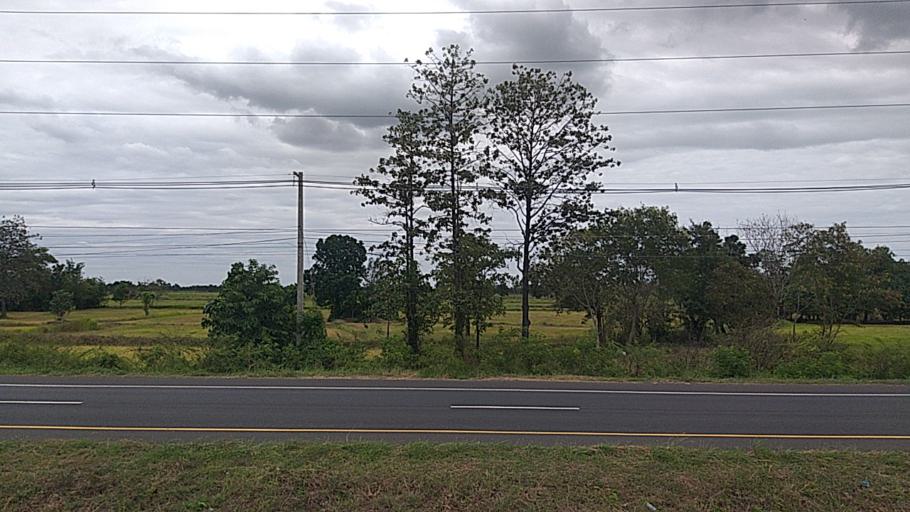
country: TH
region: Buriram
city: Prakhon Chai
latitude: 14.6096
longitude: 103.0500
